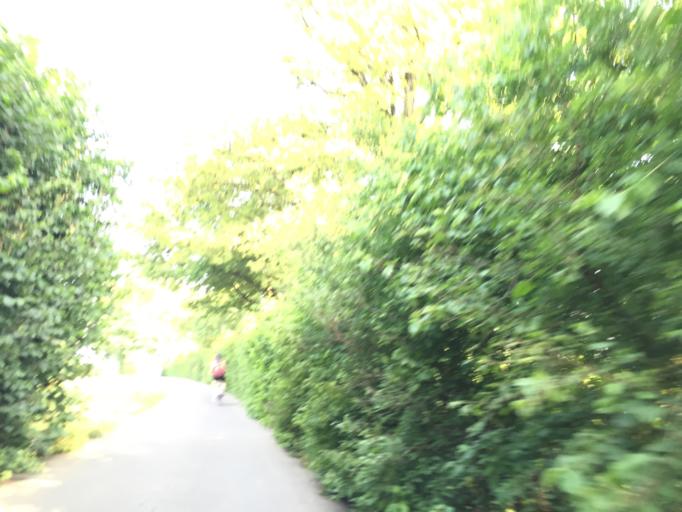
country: CH
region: Bern
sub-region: Bern-Mittelland District
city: Muri
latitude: 46.9410
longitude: 7.4848
